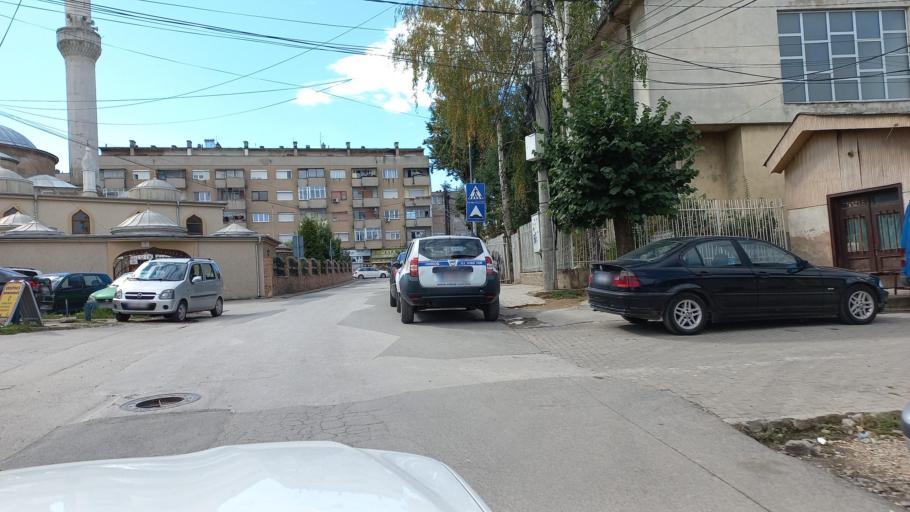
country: MK
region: Kumanovo
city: Kumanovo
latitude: 42.1380
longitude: 21.7145
